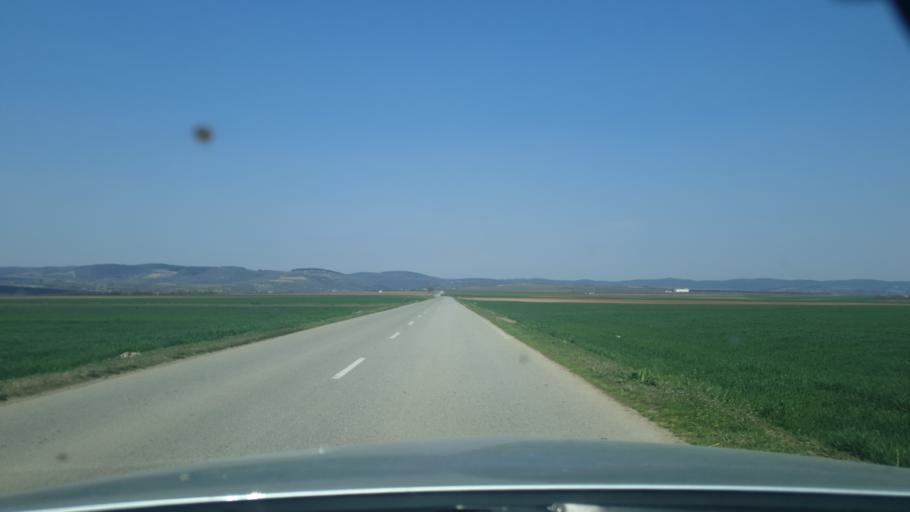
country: RS
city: Vrdnik
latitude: 45.0701
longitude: 19.7697
